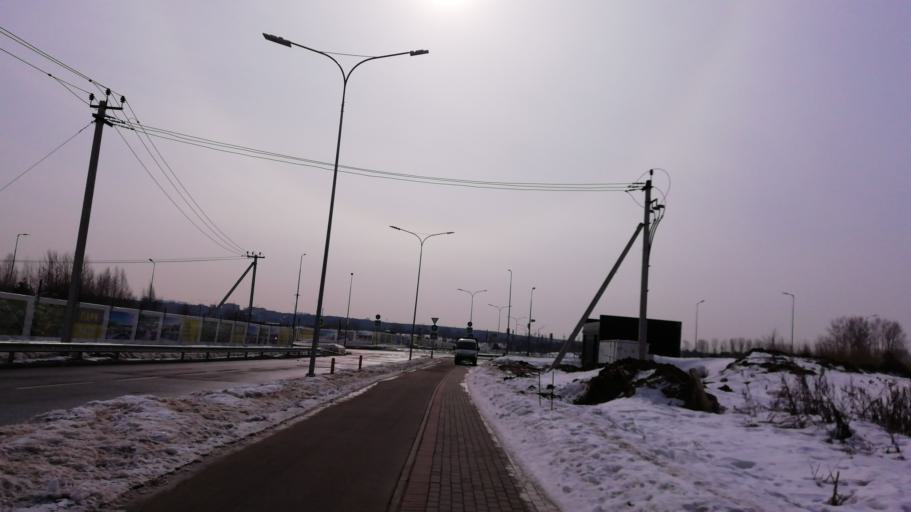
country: RU
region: Moskovskaya
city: Novoivanovskoye
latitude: 55.7000
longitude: 37.3661
